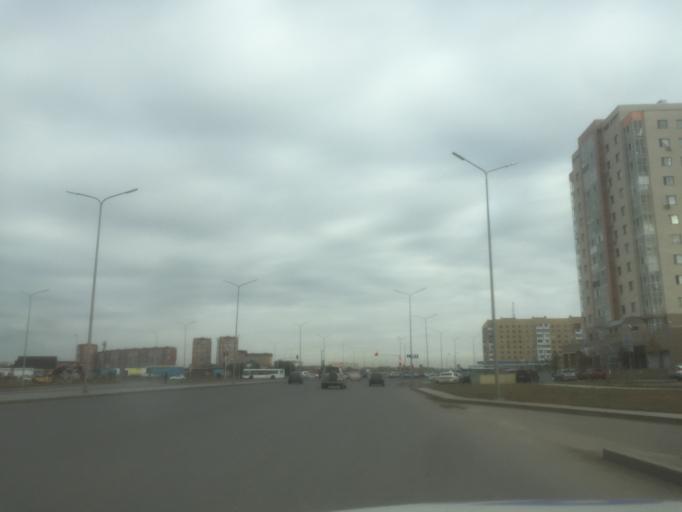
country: KZ
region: Astana Qalasy
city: Astana
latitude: 51.1705
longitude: 71.3768
